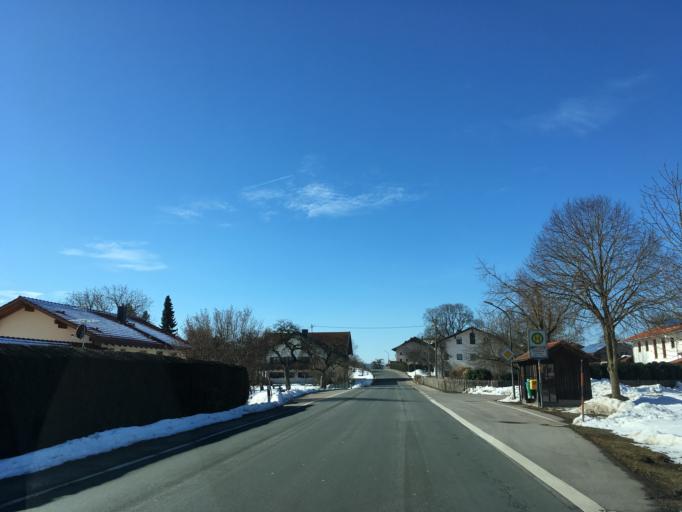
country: DE
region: Bavaria
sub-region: Upper Bavaria
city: Albaching
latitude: 48.1122
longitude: 12.1278
